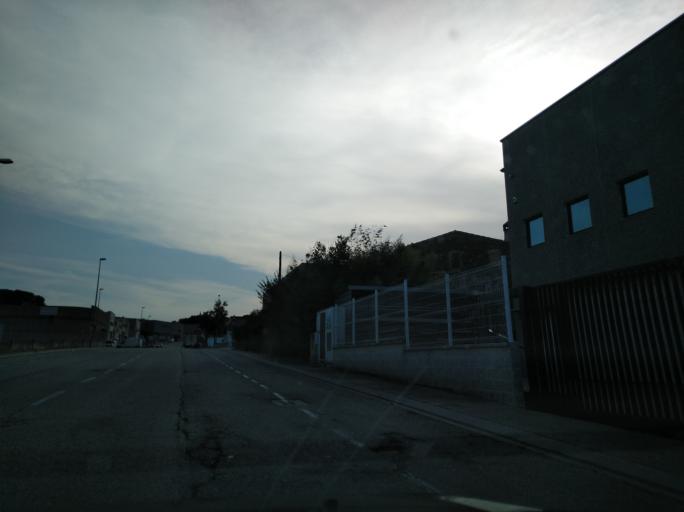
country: ES
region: Catalonia
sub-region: Provincia de Girona
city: Vilablareix
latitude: 41.9430
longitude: 2.7805
